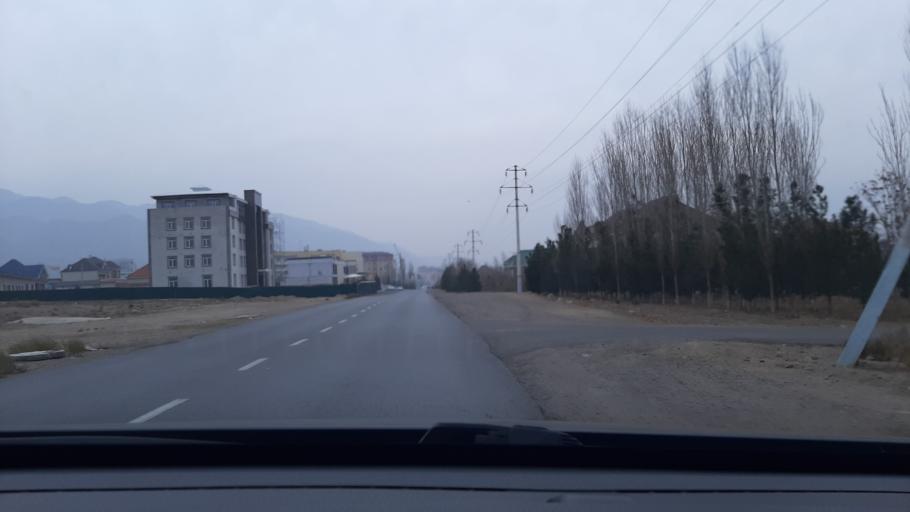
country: TJ
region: Viloyati Sughd
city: Khujand
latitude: 40.2779
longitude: 69.5820
